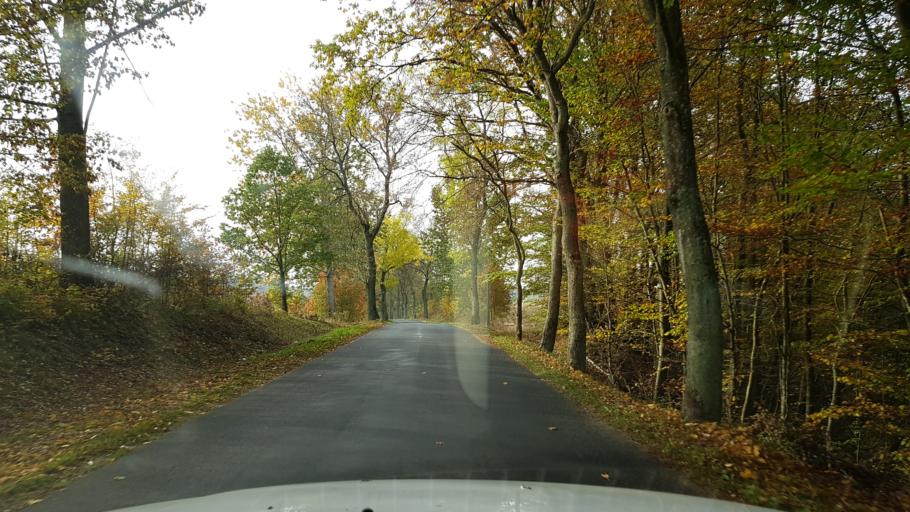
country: PL
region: West Pomeranian Voivodeship
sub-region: Powiat swidwinski
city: Polczyn-Zdroj
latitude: 53.7561
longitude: 16.0613
